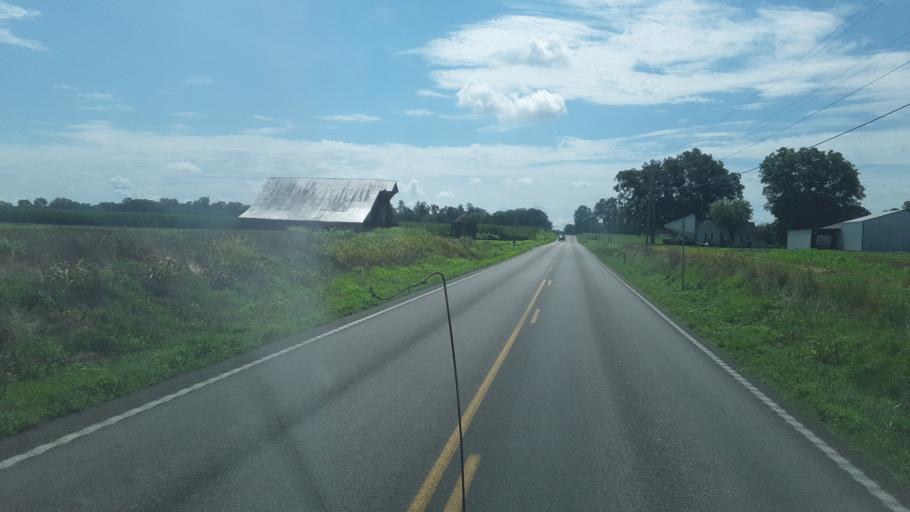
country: US
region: Kentucky
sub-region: Christian County
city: Oak Grove
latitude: 36.7646
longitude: -87.3278
